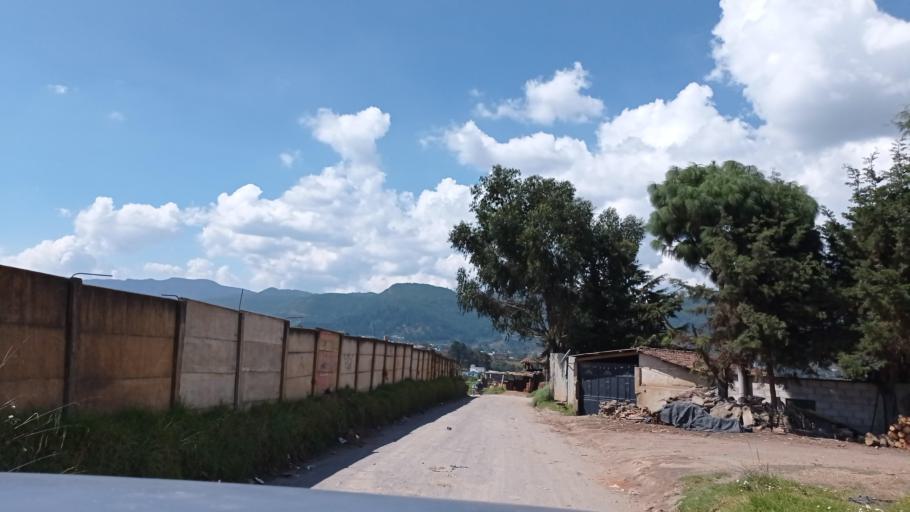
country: GT
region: Quetzaltenango
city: Olintepeque
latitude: 14.8726
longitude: -91.4926
